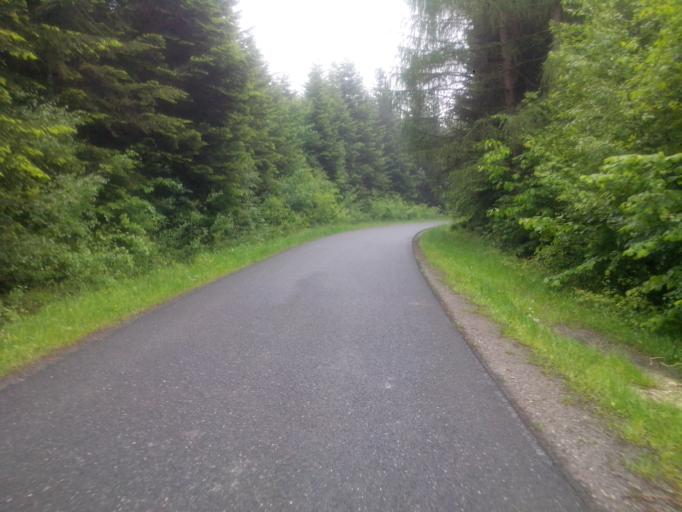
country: PL
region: Subcarpathian Voivodeship
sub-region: Powiat strzyzowski
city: Wysoka Strzyzowska
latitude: 49.8198
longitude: 21.7884
